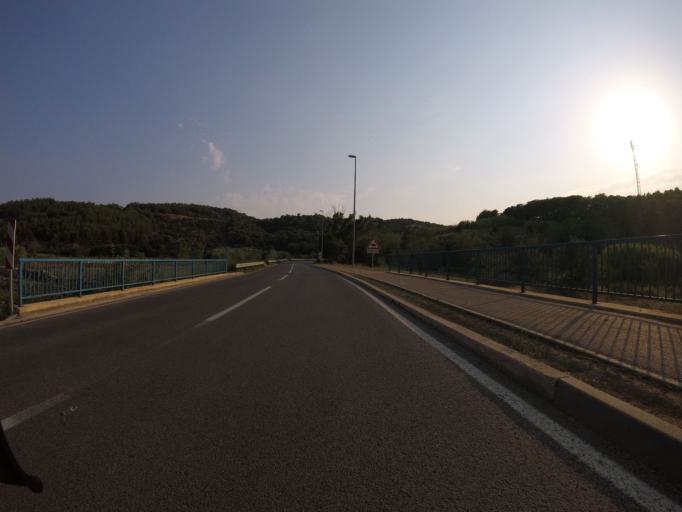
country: HR
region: Primorsko-Goranska
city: Lopar
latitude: 44.8279
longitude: 14.7279
